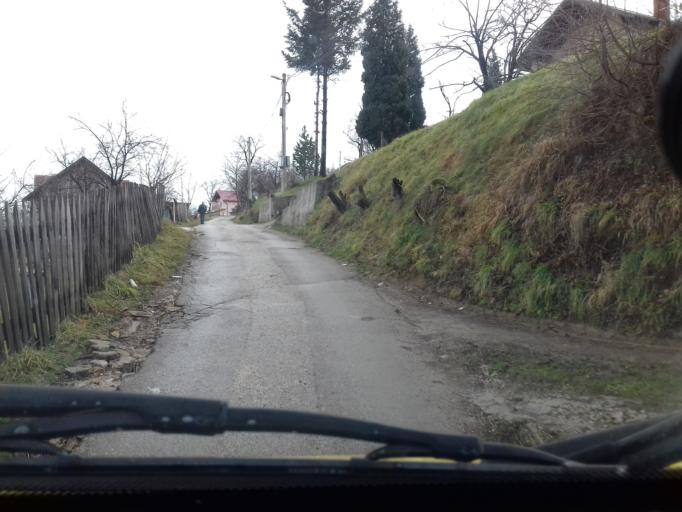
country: BA
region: Federation of Bosnia and Herzegovina
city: Zenica
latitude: 44.1840
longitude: 17.9465
